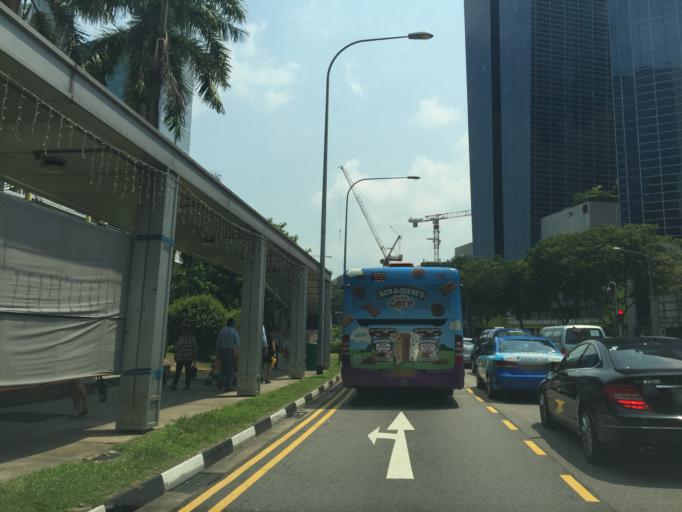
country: SG
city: Singapore
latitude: 1.3182
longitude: 103.8440
